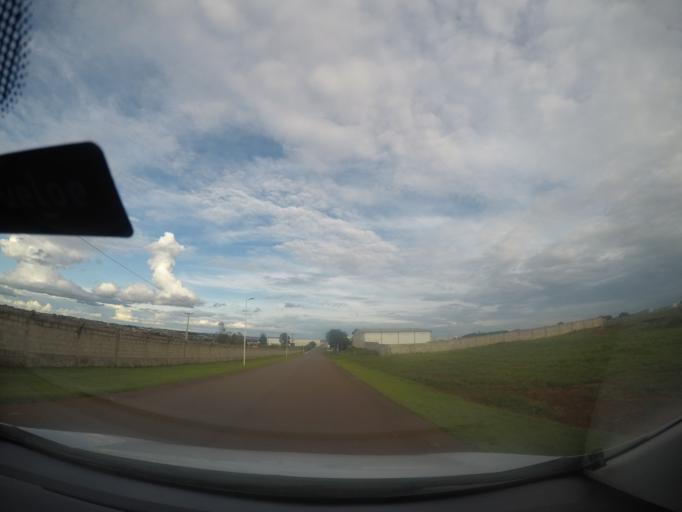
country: BR
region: Goias
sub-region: Goiania
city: Goiania
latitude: -16.6229
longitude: -49.3522
